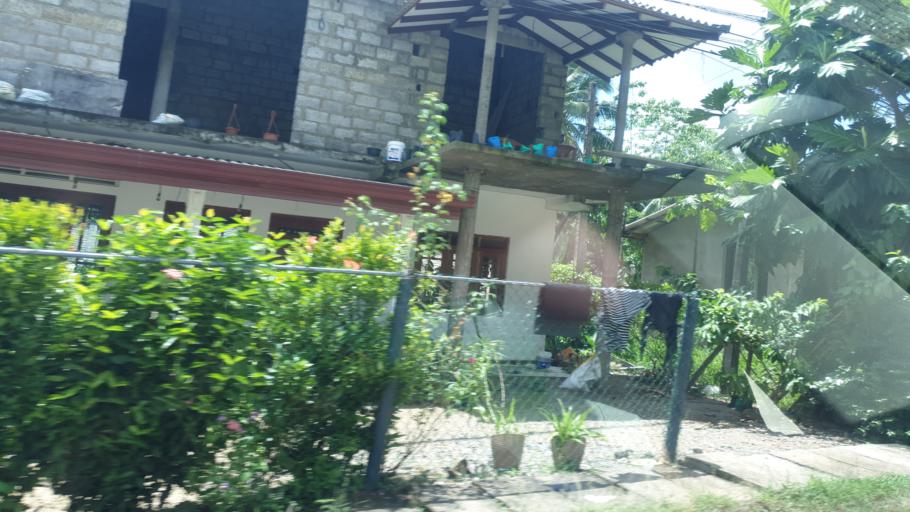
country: LK
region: Western
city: Horawala Junction
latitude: 6.5238
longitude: 80.2158
